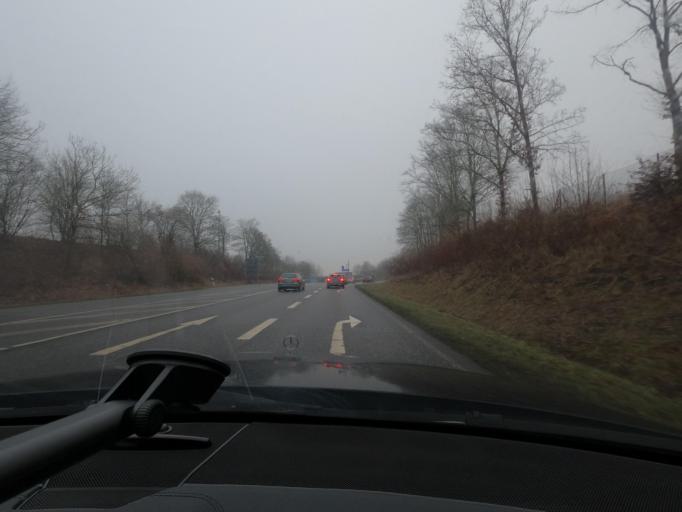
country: DE
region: Hesse
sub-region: Regierungsbezirk Kassel
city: Martinhagen
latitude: 51.3197
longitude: 9.2813
